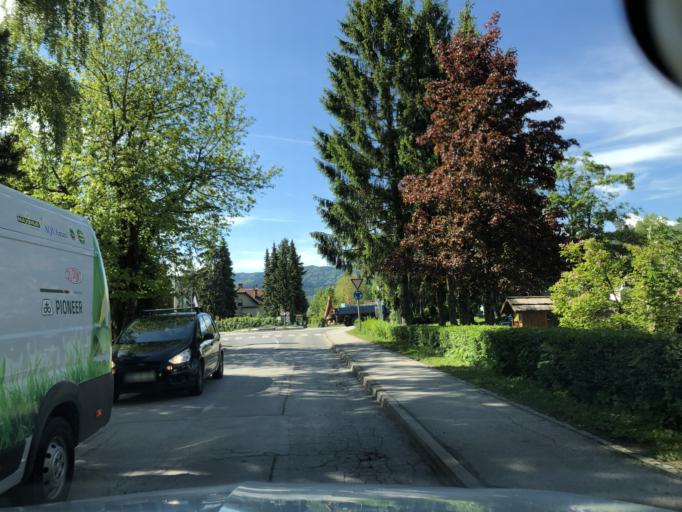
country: SI
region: Bled
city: Bled
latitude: 46.3692
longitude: 14.1164
